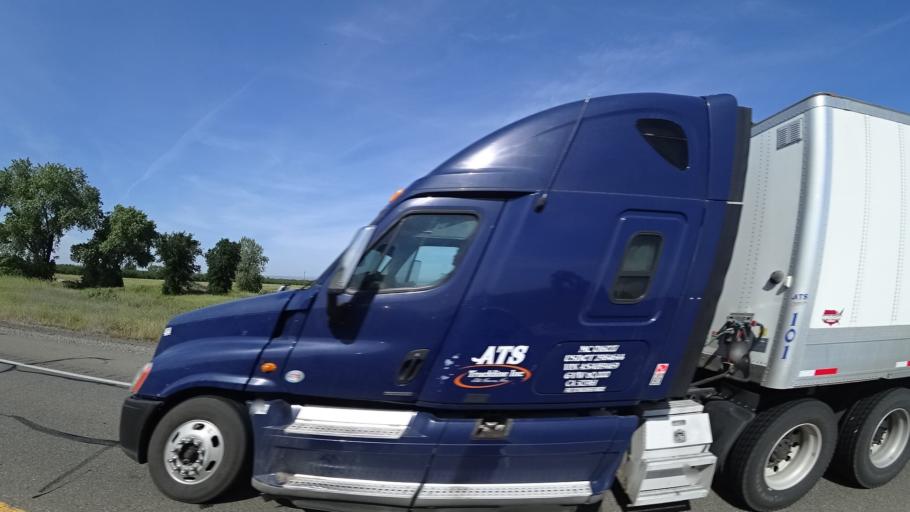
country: US
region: California
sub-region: Tehama County
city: Los Molinos
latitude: 39.9349
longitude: -122.0367
